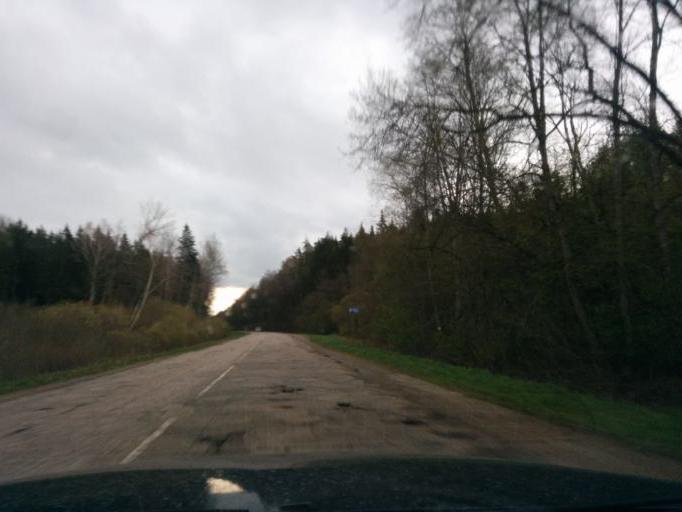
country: LT
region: Siauliu apskritis
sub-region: Joniskis
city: Joniskis
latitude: 56.4161
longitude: 23.6233
